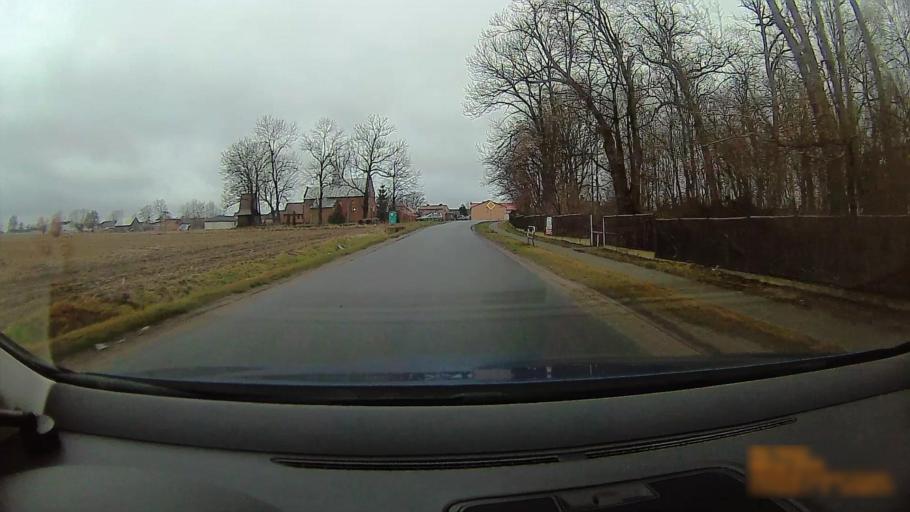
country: PL
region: Greater Poland Voivodeship
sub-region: Powiat koninski
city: Rychwal
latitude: 52.0960
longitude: 18.1436
